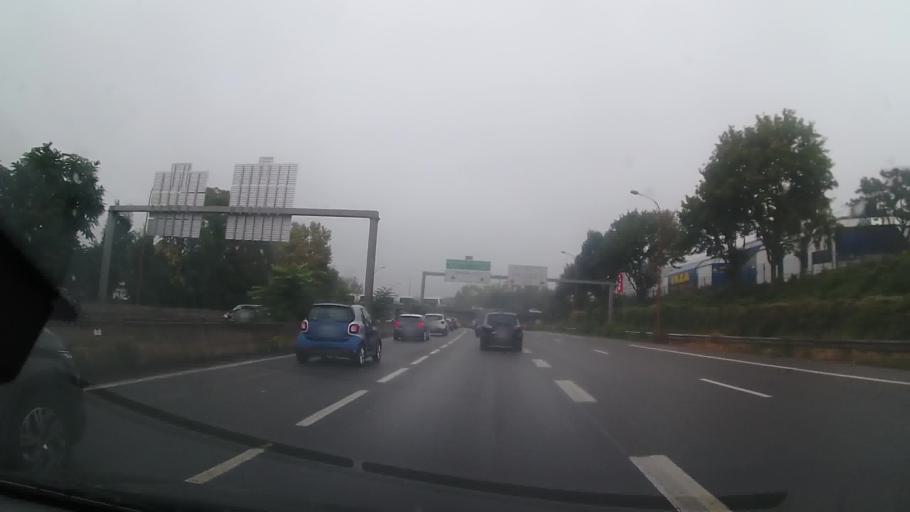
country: FR
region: Ile-de-France
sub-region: Departement de l'Essonne
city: Bievres
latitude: 48.7827
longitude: 2.2234
